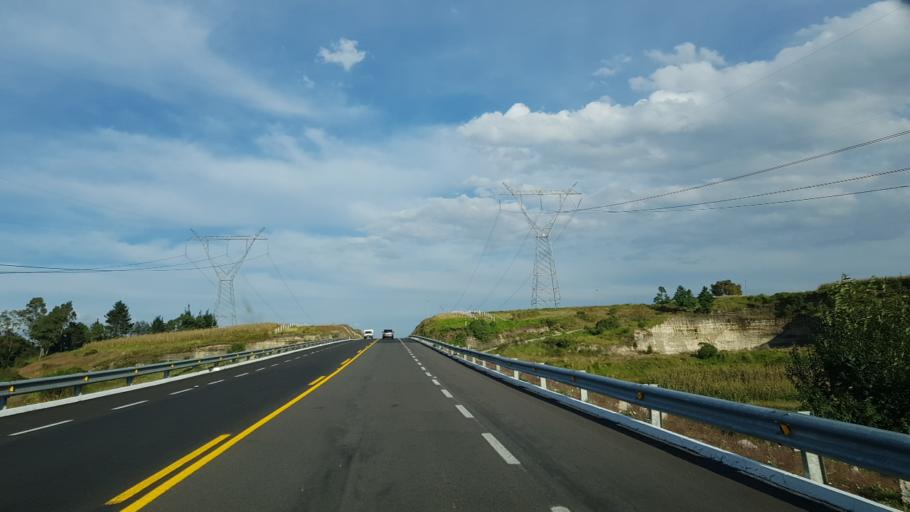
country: MX
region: Mexico
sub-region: Almoloya de Juarez
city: San Pedro de la Hortaliza (Ejido Almoloyan)
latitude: 19.3784
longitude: -99.8366
